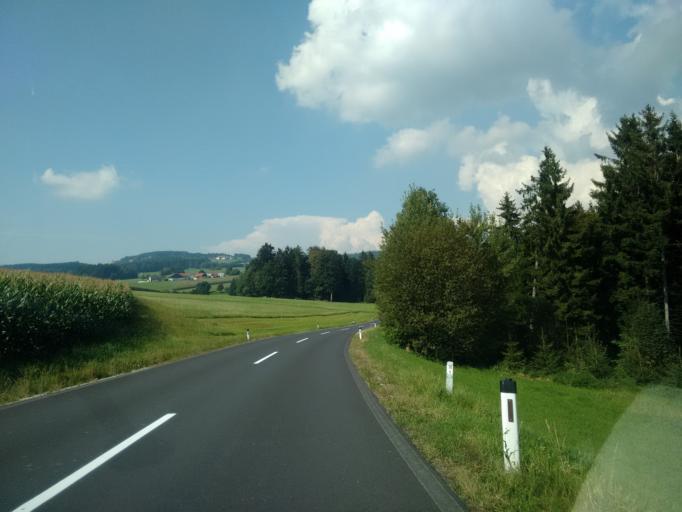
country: AT
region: Upper Austria
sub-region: Politischer Bezirk Urfahr-Umgebung
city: Altenberg bei Linz
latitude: 48.3978
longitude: 14.3447
